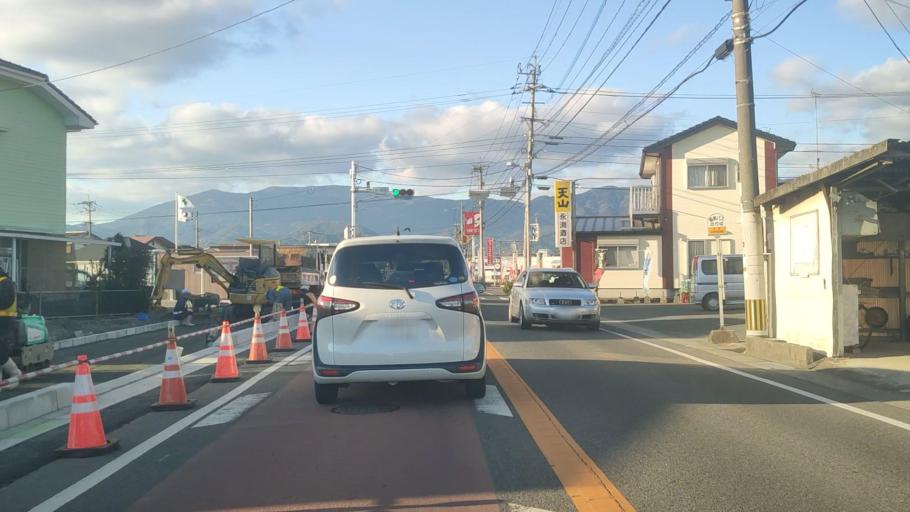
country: JP
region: Saga Prefecture
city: Saga-shi
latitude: 33.2749
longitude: 130.2171
